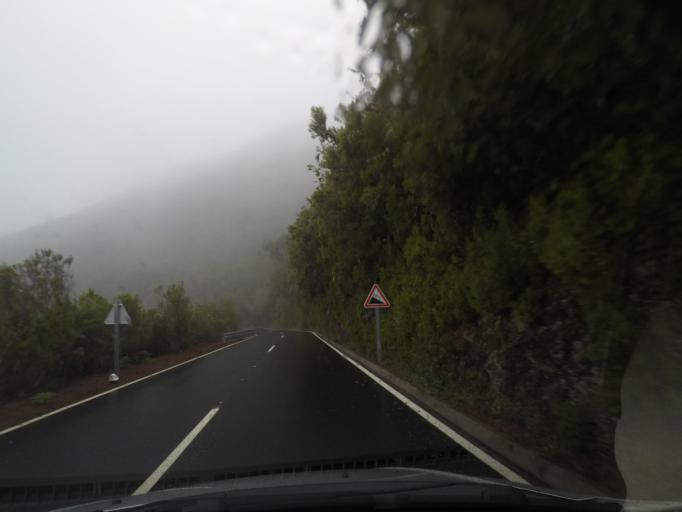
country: PT
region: Madeira
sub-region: Santana
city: Santana
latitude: 32.7689
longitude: -16.9169
